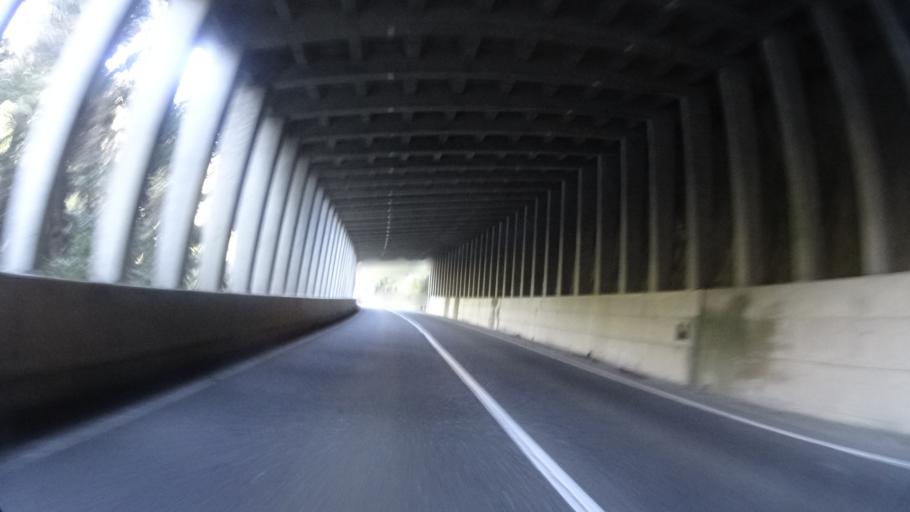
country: JP
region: Fukui
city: Maruoka
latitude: 36.2157
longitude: 136.3528
